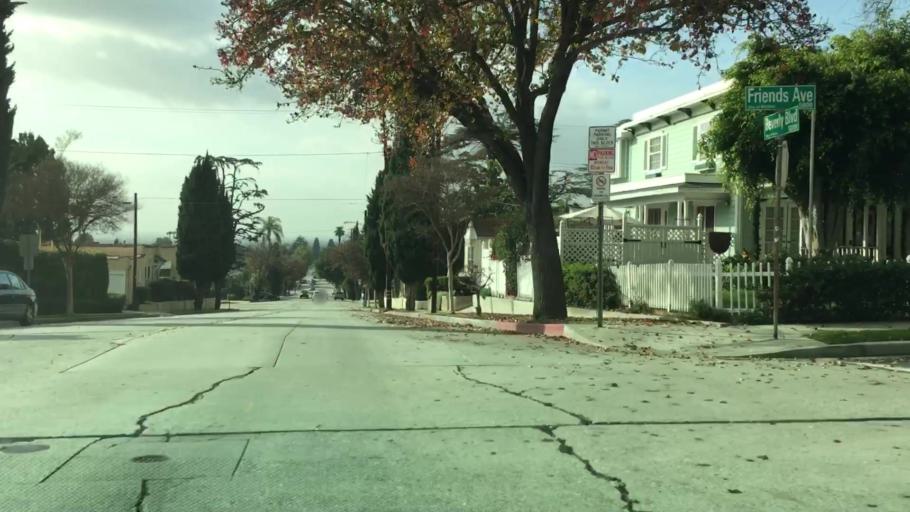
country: US
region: California
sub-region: Los Angeles County
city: Whittier
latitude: 33.9881
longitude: -118.0339
